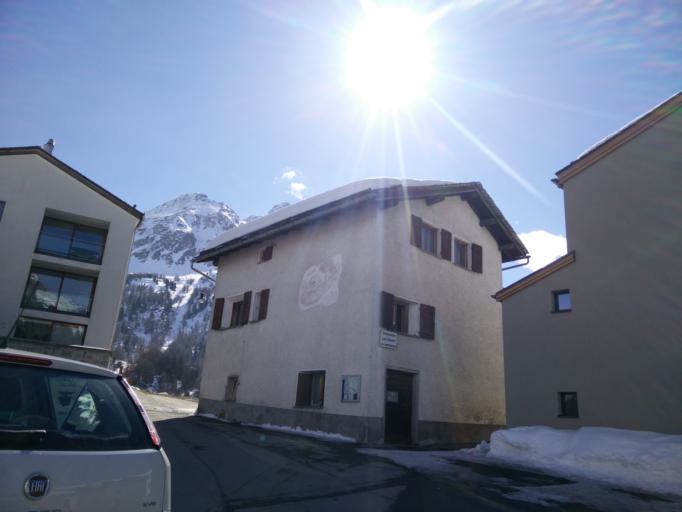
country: CH
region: Grisons
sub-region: Maloja District
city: Silvaplana
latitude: 46.3997
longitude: 9.6961
